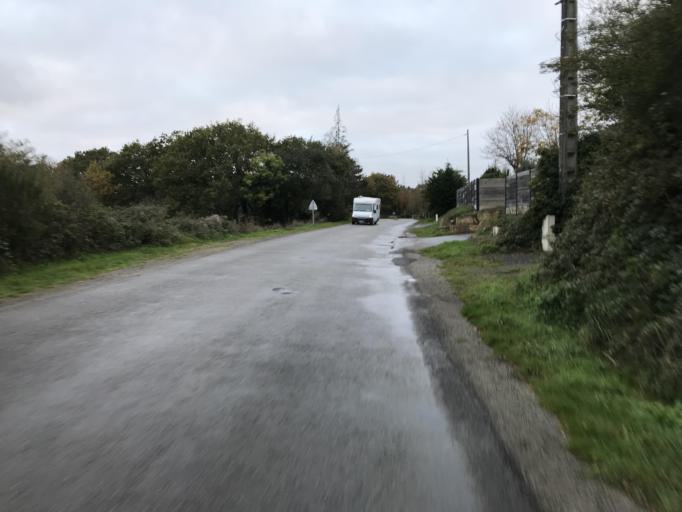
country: FR
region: Brittany
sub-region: Departement du Finistere
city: Logonna-Daoulas
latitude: 48.3201
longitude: -4.3143
